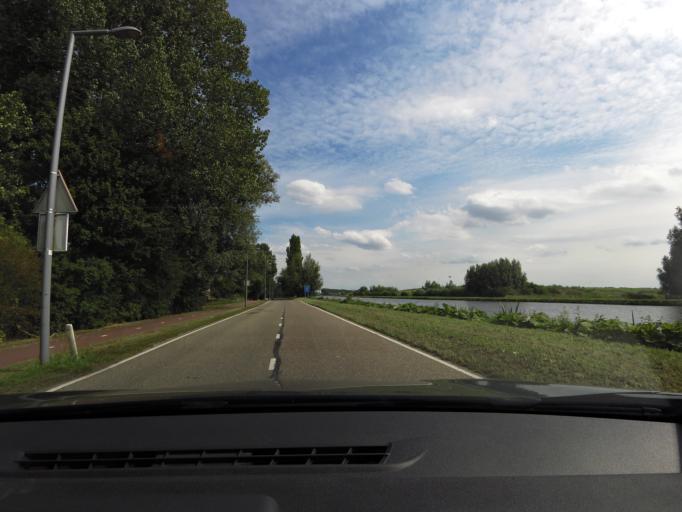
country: NL
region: South Holland
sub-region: Gemeente Schiedam
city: Schiedam
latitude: 51.9565
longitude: 4.3996
